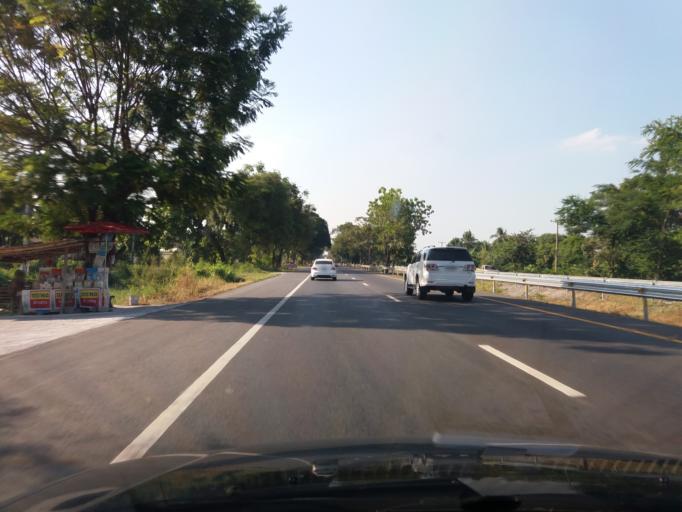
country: TH
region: Nakhon Sawan
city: Kao Liao
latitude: 15.7998
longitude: 99.9574
